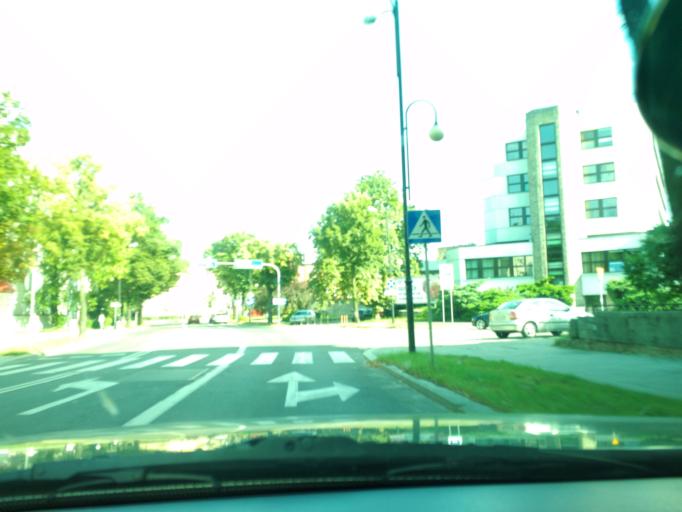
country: PL
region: Silesian Voivodeship
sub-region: Gliwice
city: Gliwice
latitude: 50.2896
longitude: 18.6605
